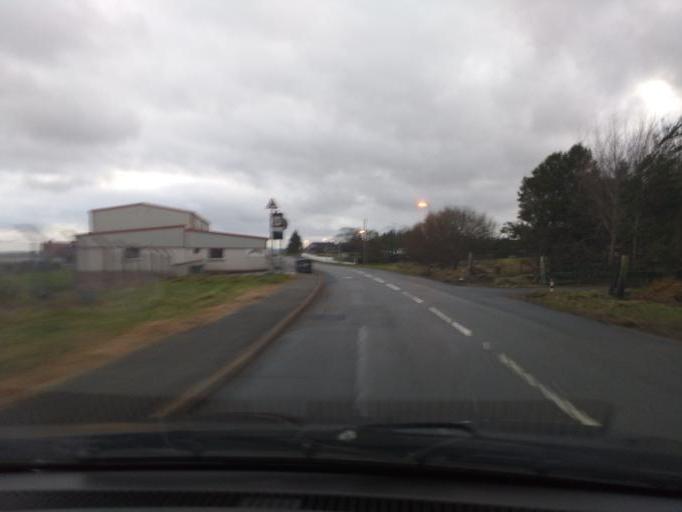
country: GB
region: Scotland
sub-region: Eilean Siar
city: Isle of Lewis
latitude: 58.2455
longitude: -6.3485
